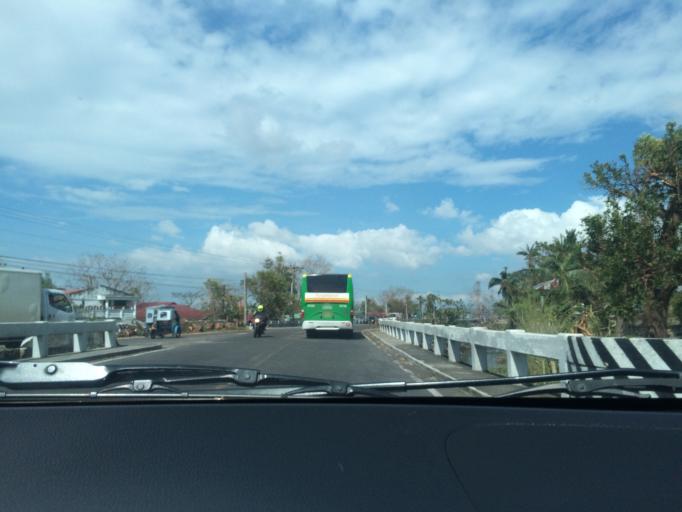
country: PH
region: Bicol
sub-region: Province of Albay
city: Iraya
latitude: 13.2618
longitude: 123.4972
